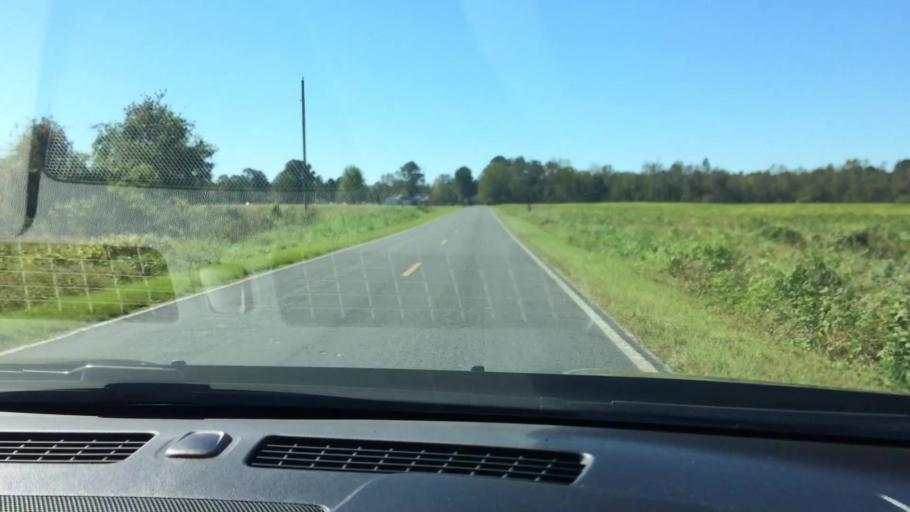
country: US
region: North Carolina
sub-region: Pitt County
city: Grifton
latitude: 35.2970
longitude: -77.3242
